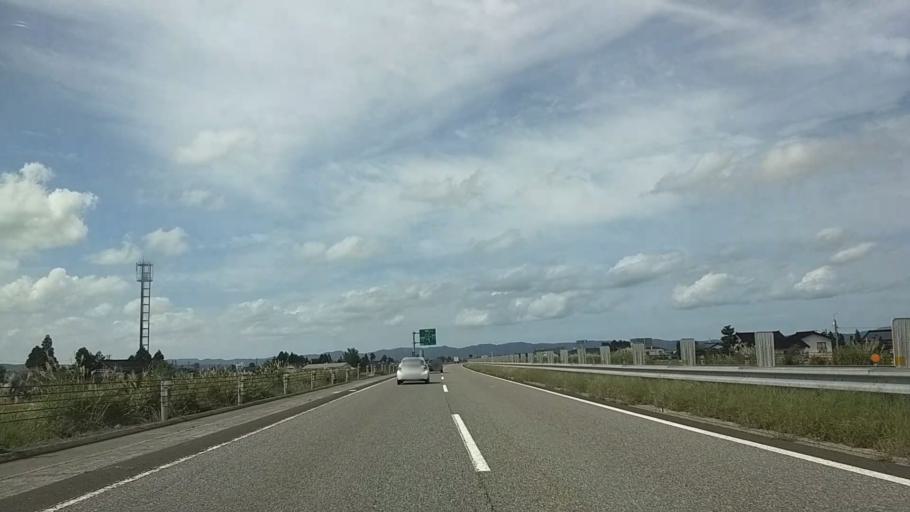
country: JP
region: Toyama
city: Nanto-shi
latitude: 36.6238
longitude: 136.9345
